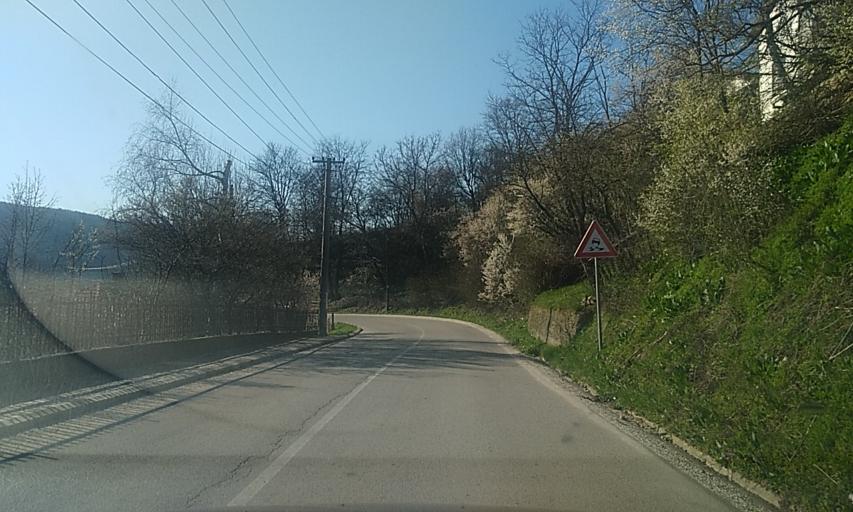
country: RS
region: Central Serbia
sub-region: Pcinjski Okrug
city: Bosilegrad
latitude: 42.4836
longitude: 22.4740
